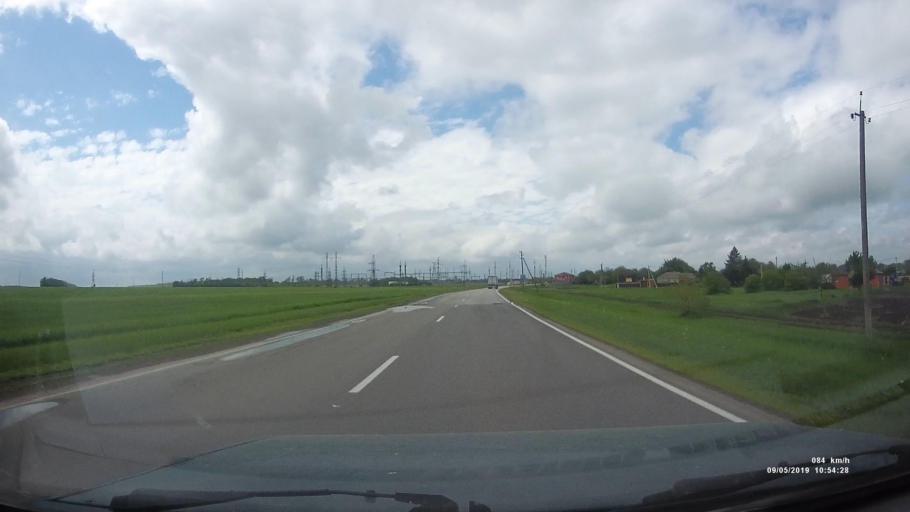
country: RU
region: Rostov
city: Peshkovo
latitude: 46.8774
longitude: 39.3301
